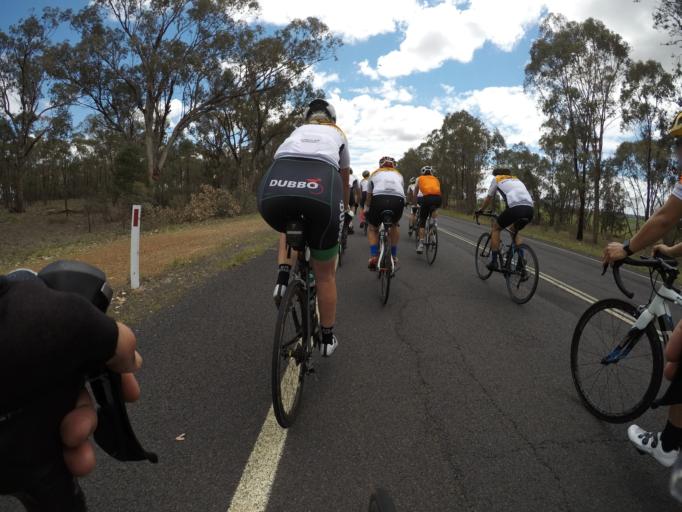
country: AU
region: New South Wales
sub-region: Dubbo Municipality
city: Dubbo
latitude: -32.4146
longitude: 148.5708
